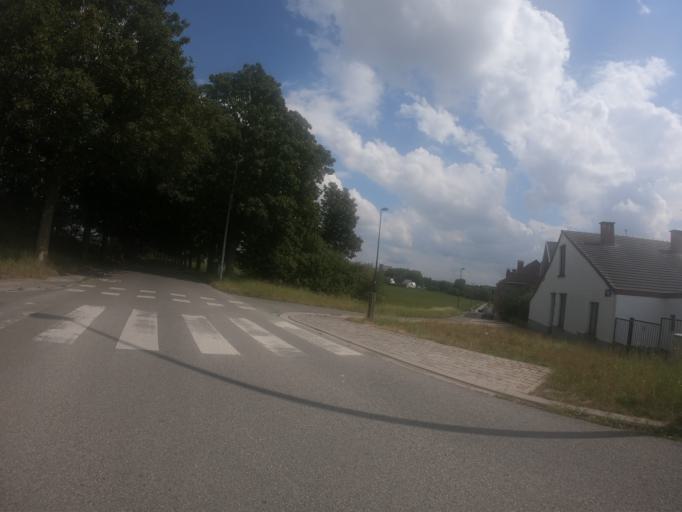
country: BE
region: Flanders
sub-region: Provincie Vlaams-Brabant
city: Dilbeek
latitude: 50.8328
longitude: 4.2718
